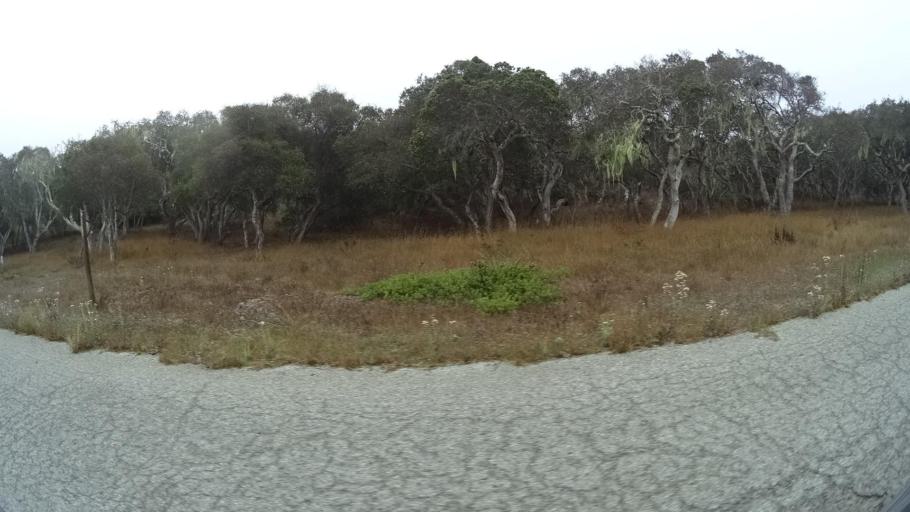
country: US
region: California
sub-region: Monterey County
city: Marina
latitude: 36.6458
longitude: -121.7638
